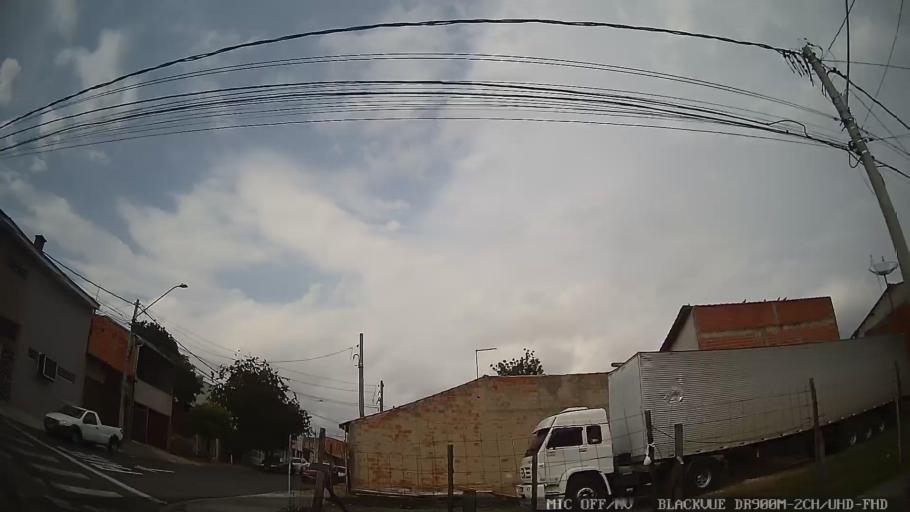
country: BR
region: Sao Paulo
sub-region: Indaiatuba
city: Indaiatuba
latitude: -23.1276
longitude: -47.2443
